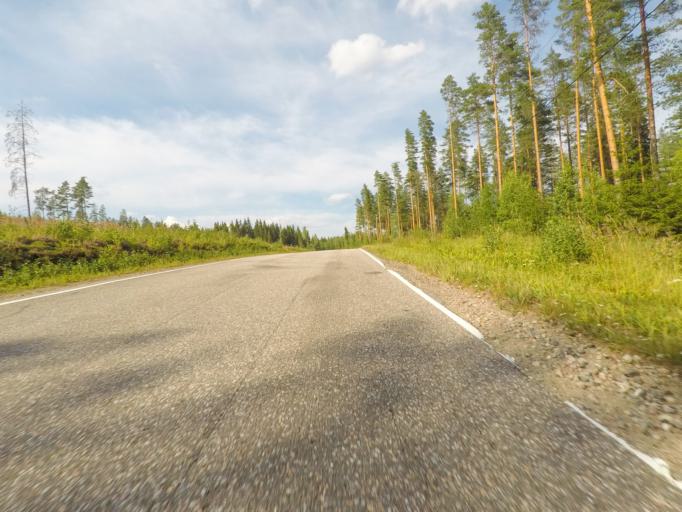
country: FI
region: Southern Savonia
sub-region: Savonlinna
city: Sulkava
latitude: 61.7753
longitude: 28.2392
